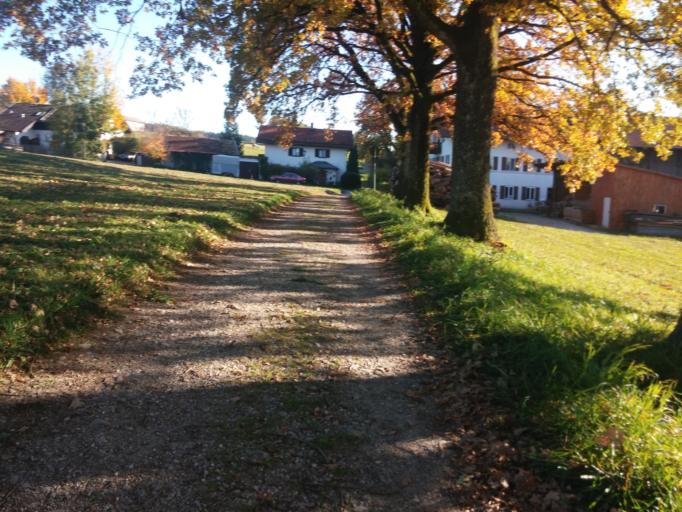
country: DE
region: Bavaria
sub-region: Upper Bavaria
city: Aying
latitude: 47.9690
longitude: 11.7814
